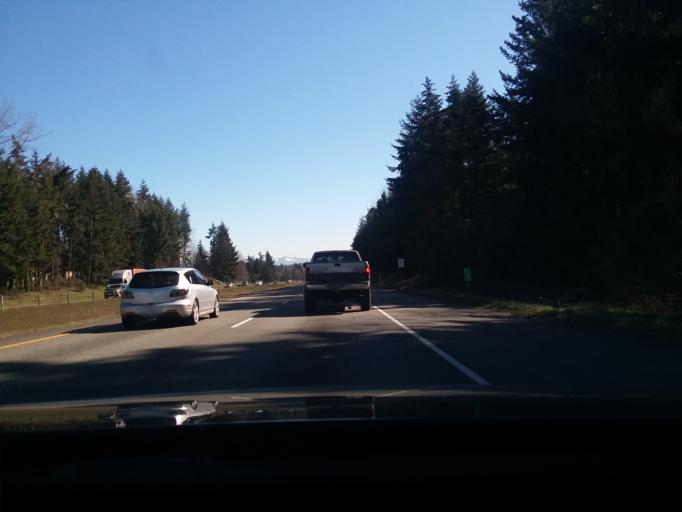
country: US
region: Washington
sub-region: Pierce County
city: Summit
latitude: 47.1580
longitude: -122.3333
